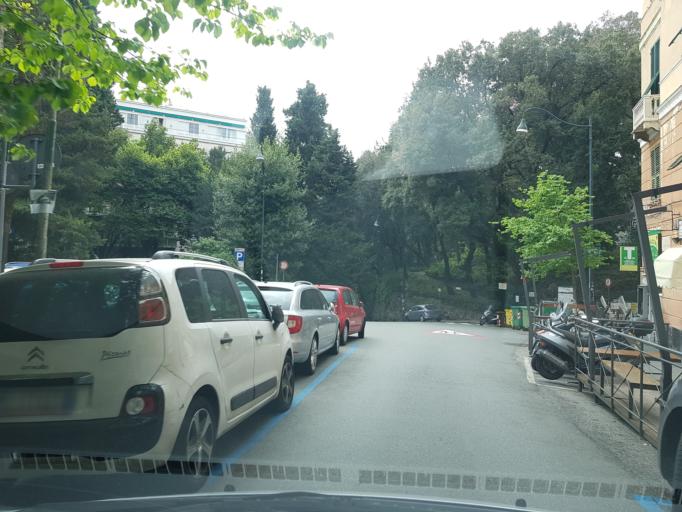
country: IT
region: Liguria
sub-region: Provincia di Genova
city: Genoa
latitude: 44.4124
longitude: 8.9370
